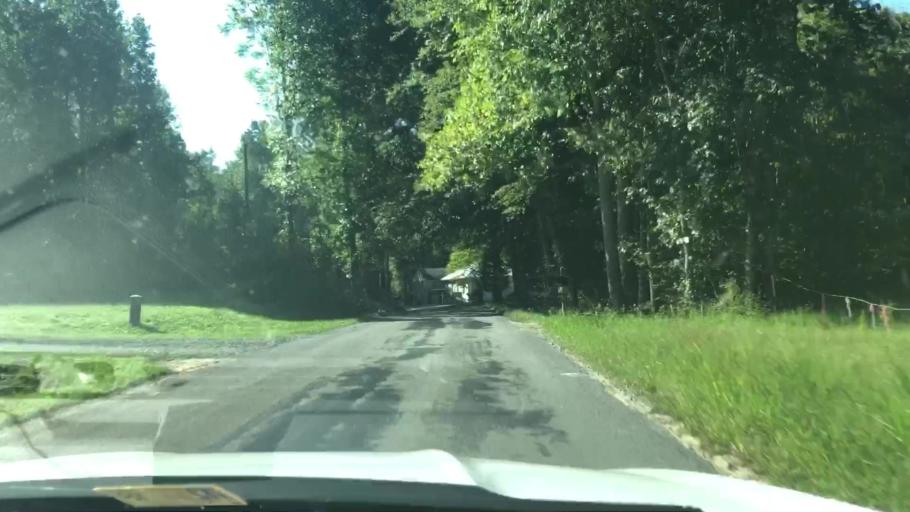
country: US
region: Virginia
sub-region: New Kent County
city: New Kent
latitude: 37.4774
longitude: -76.9333
